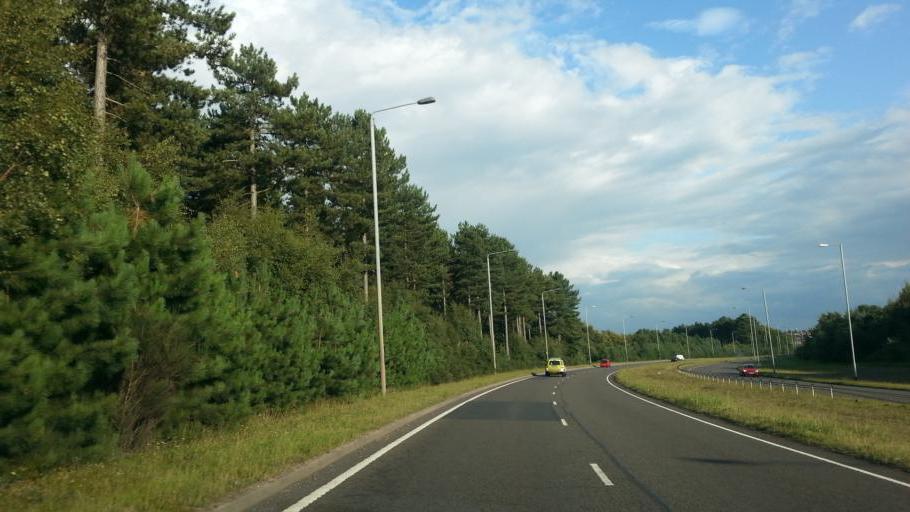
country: GB
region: England
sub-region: Nottinghamshire
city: Rainworth
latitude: 53.1297
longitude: -1.1291
